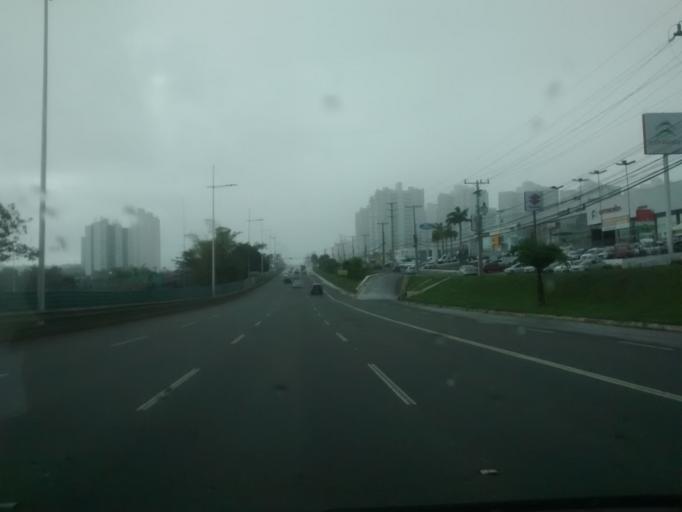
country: BR
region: Bahia
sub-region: Lauro De Freitas
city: Lauro de Freitas
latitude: -12.9393
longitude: -38.4118
